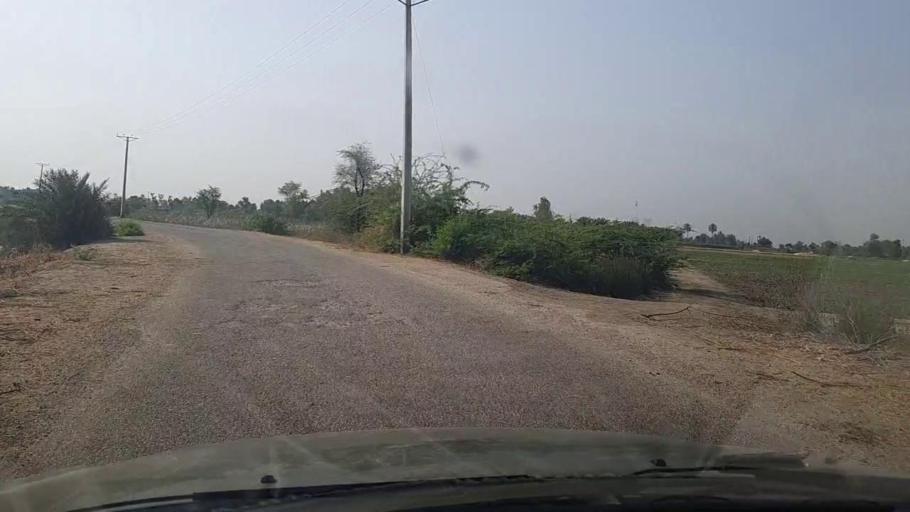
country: PK
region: Sindh
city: Kot Diji
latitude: 27.2848
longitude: 68.6483
